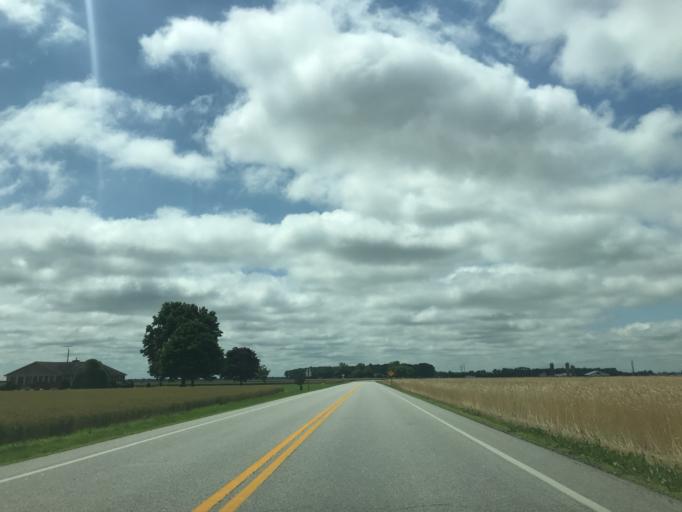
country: US
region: Maryland
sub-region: Caroline County
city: Ridgely
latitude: 38.9341
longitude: -75.8945
